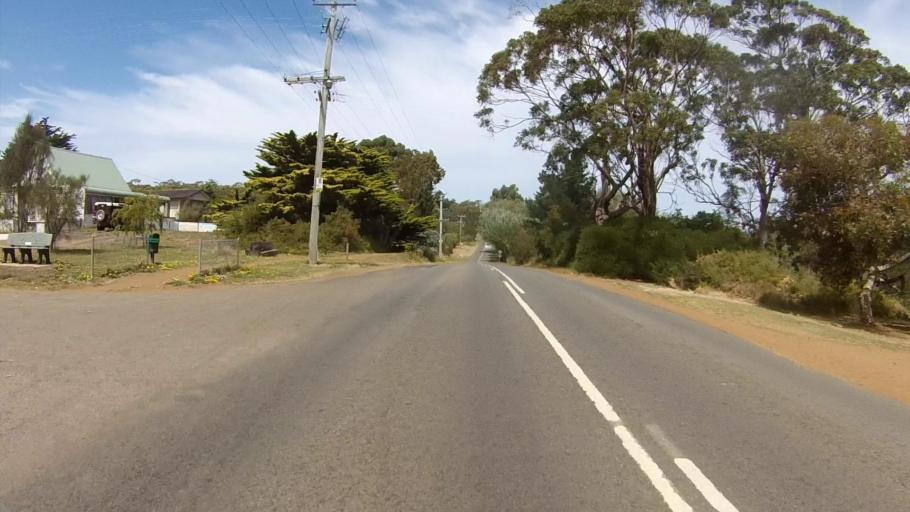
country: AU
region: Tasmania
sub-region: Kingborough
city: Taroona
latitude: -43.0123
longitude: 147.4136
